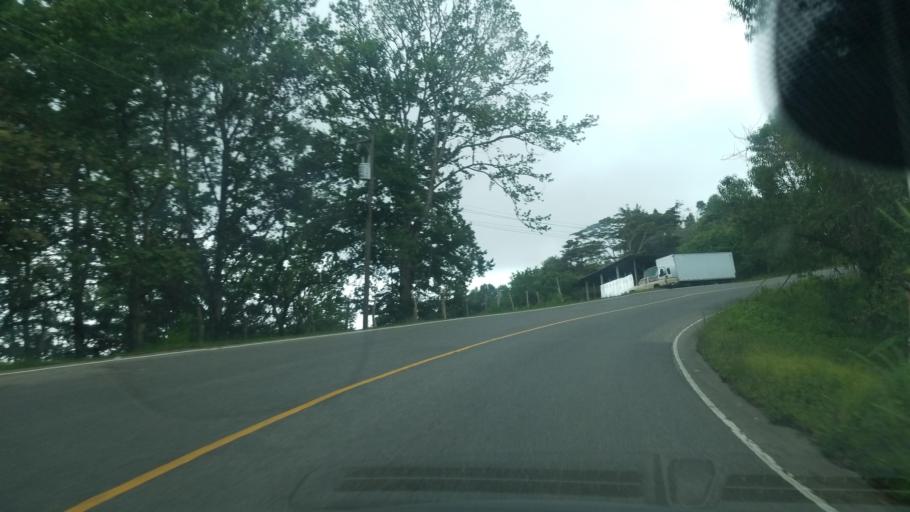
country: HN
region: Ocotepeque
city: La Labor
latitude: 14.4817
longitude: -89.0510
